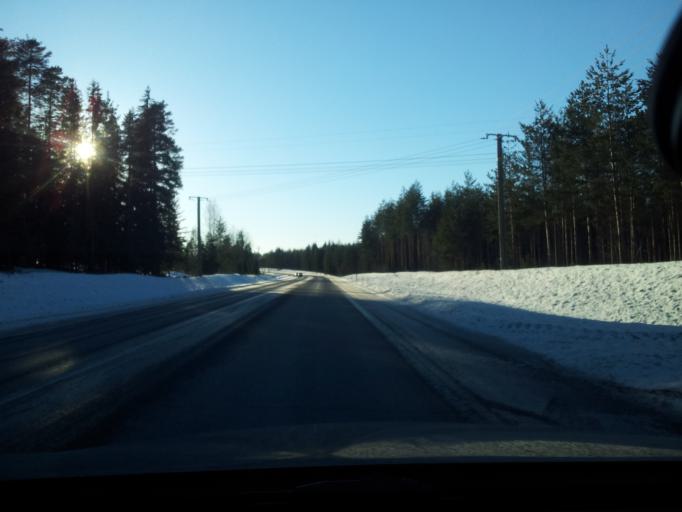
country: FI
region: Uusimaa
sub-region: Helsinki
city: Vihti
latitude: 60.3672
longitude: 24.3658
